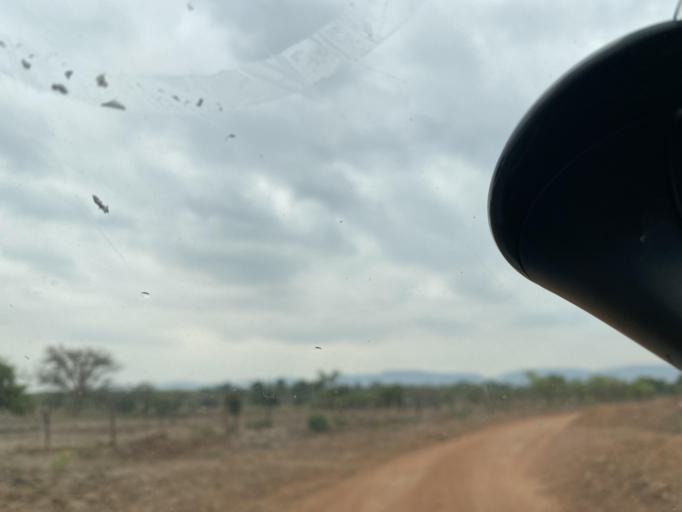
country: ZM
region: Lusaka
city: Chongwe
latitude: -15.2371
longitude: 28.7191
